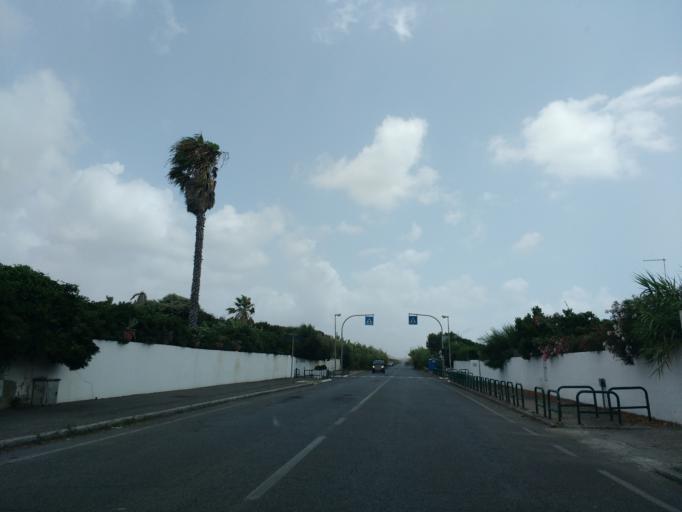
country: IT
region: Latium
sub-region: Citta metropolitana di Roma Capitale
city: Torvaianica
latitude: 41.6556
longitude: 12.4184
